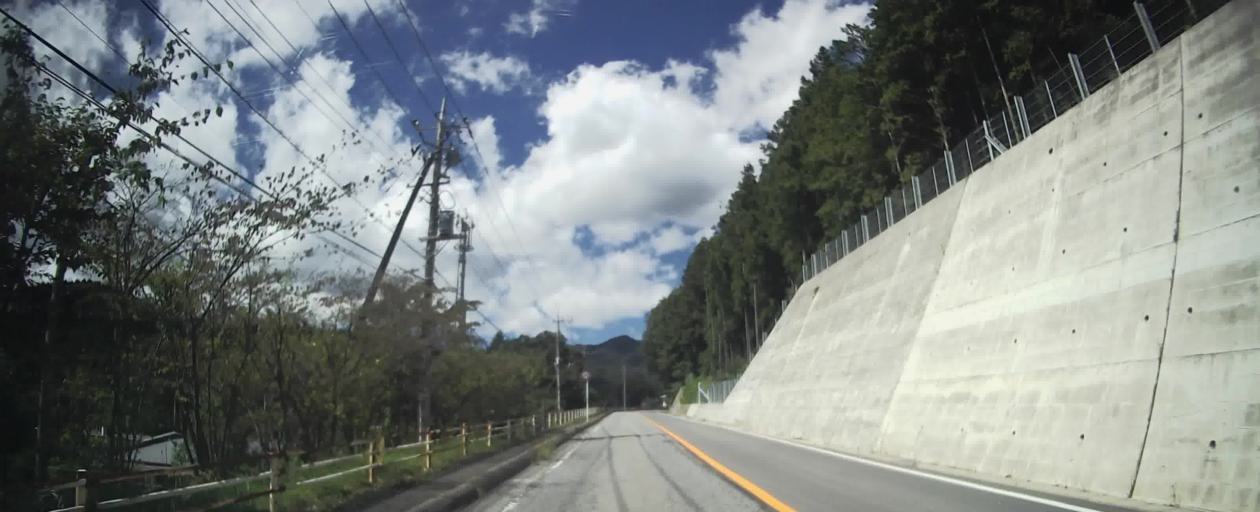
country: JP
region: Gunma
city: Kanekomachi
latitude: 36.4329
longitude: 138.9215
